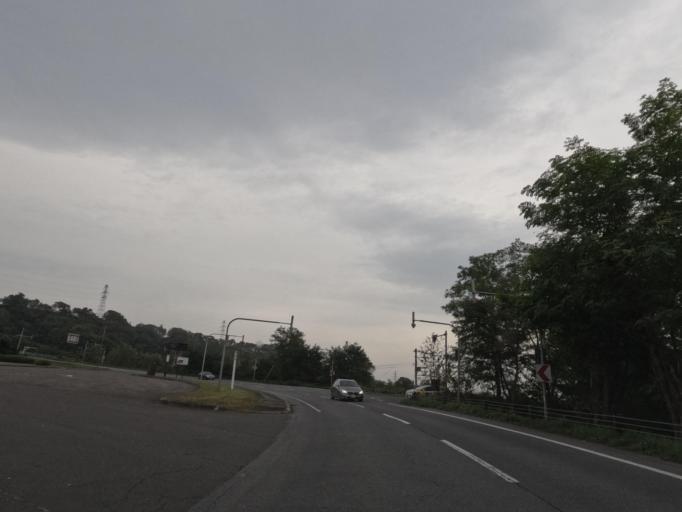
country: JP
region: Hokkaido
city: Date
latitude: 42.5094
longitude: 140.8616
